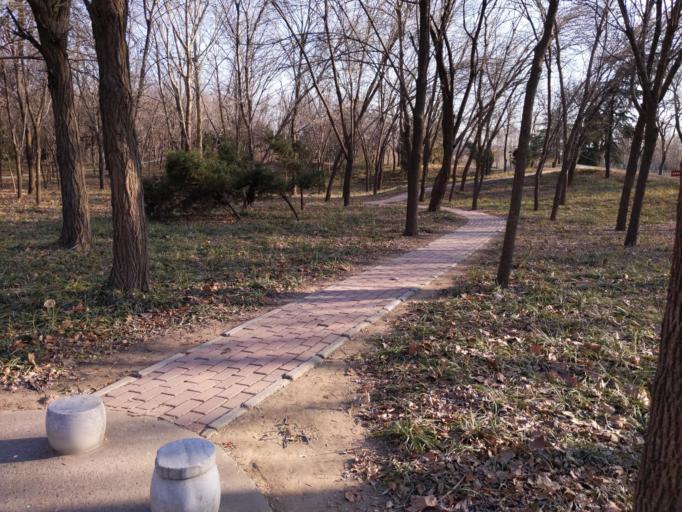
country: CN
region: Henan Sheng
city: Puyang
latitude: 35.7787
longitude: 114.9584
